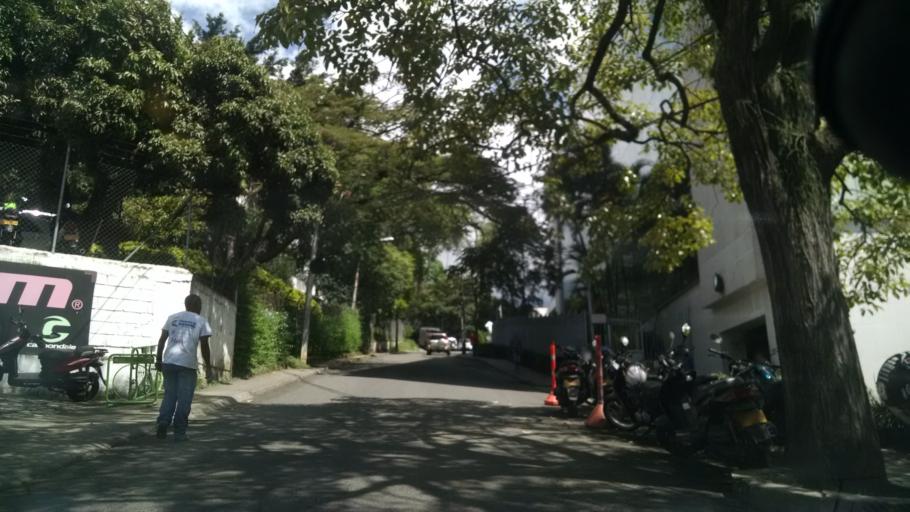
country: CO
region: Antioquia
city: Medellin
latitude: 6.2128
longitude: -75.5697
